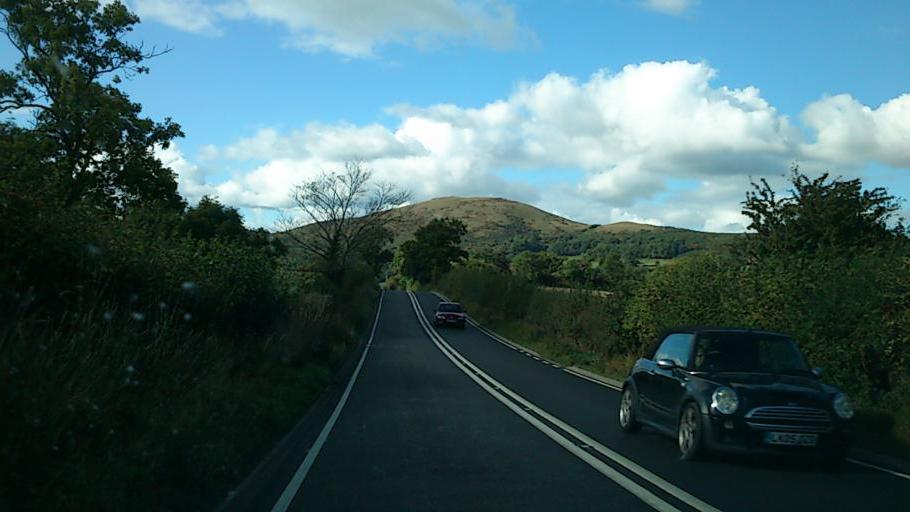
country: GB
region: England
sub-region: Shropshire
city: Westbury
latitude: 52.7043
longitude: -3.0038
